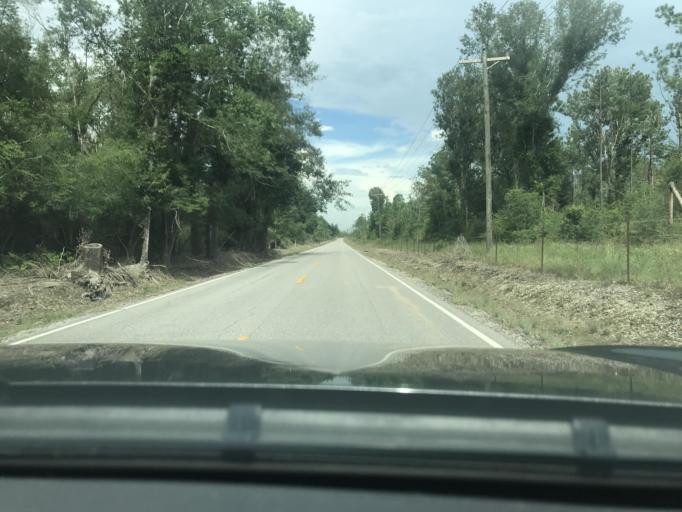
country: US
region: Louisiana
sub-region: Calcasieu Parish
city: Moss Bluff
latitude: 30.3885
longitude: -93.2411
